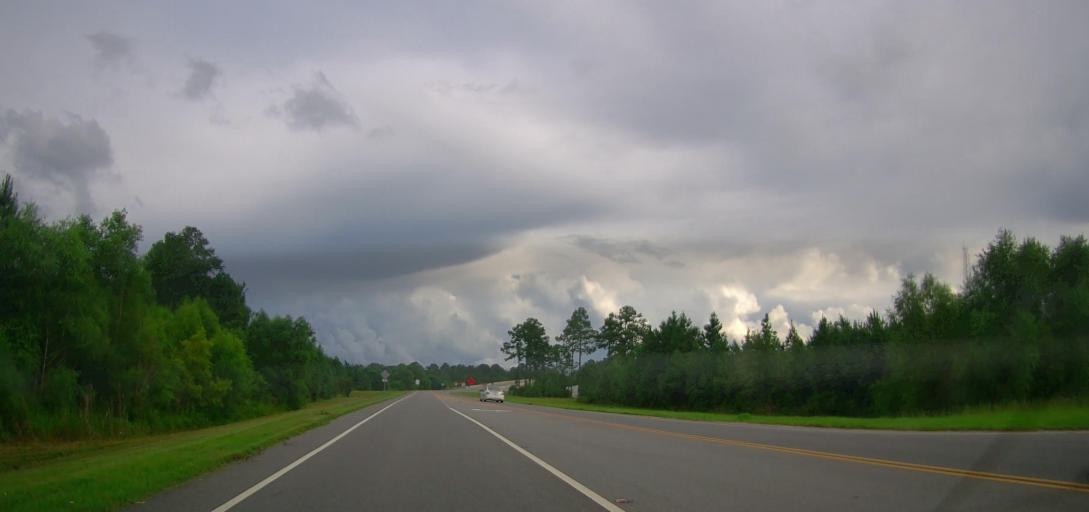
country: US
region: Georgia
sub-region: Wayne County
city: Jesup
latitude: 31.6234
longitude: -81.8977
